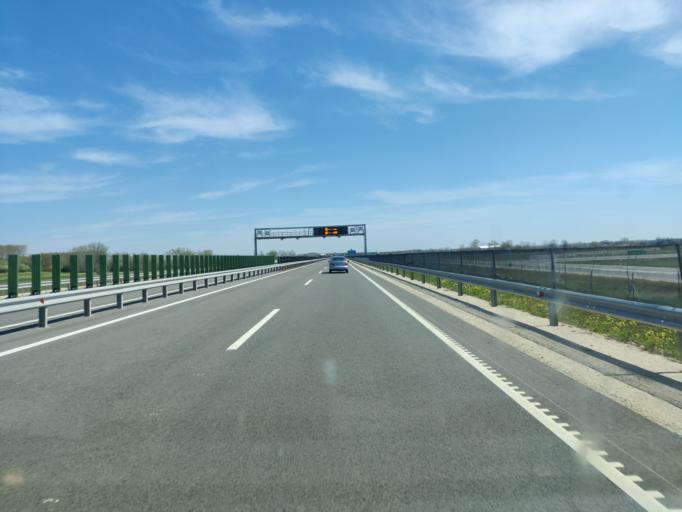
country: HU
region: Bacs-Kiskun
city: Tiszakecske
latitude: 46.8686
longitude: 20.0835
